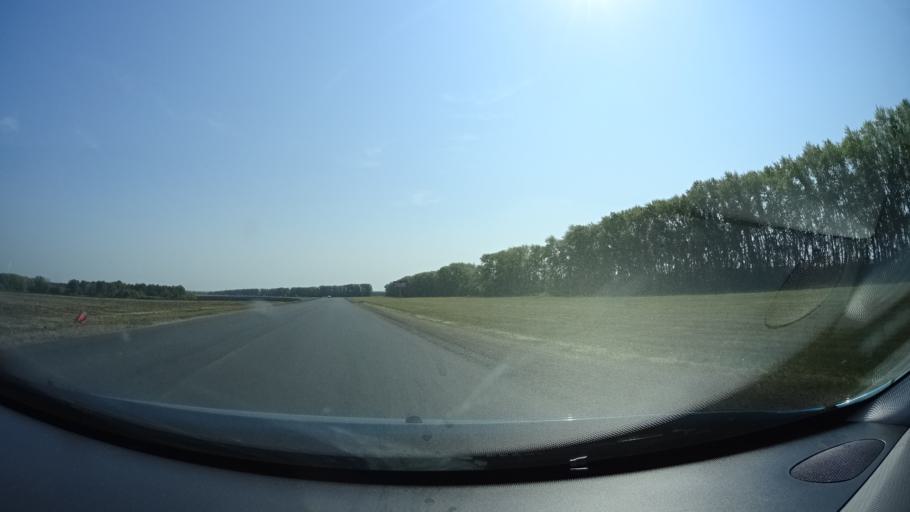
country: RU
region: Bashkortostan
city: Karmaskaly
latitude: 54.3883
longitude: 56.1306
